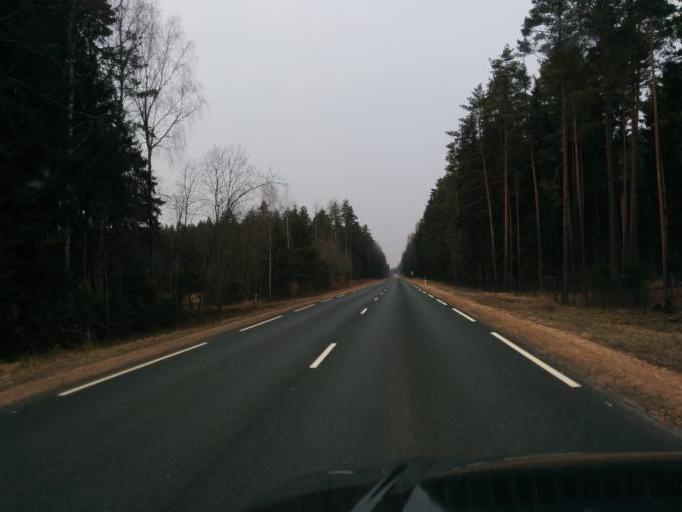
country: LV
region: Ikskile
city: Ikskile
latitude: 56.8050
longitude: 24.4977
